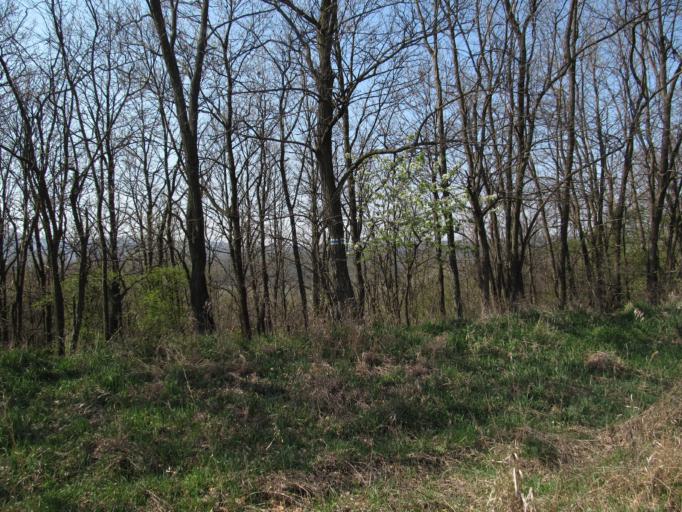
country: HU
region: Pest
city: Kosd
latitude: 47.8752
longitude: 19.1901
